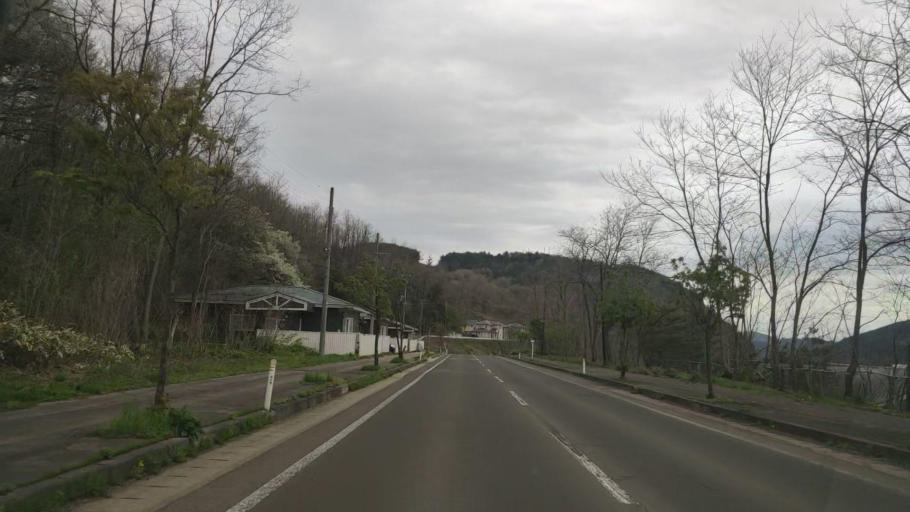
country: JP
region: Akita
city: Hanawa
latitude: 40.3281
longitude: 140.7474
